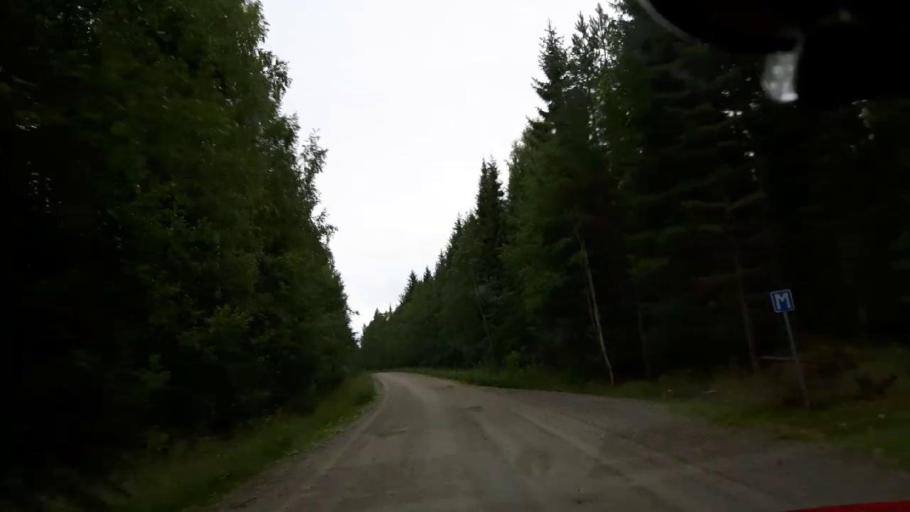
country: SE
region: Vaesternorrland
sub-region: Ange Kommun
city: Ange
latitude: 62.7975
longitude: 15.7705
